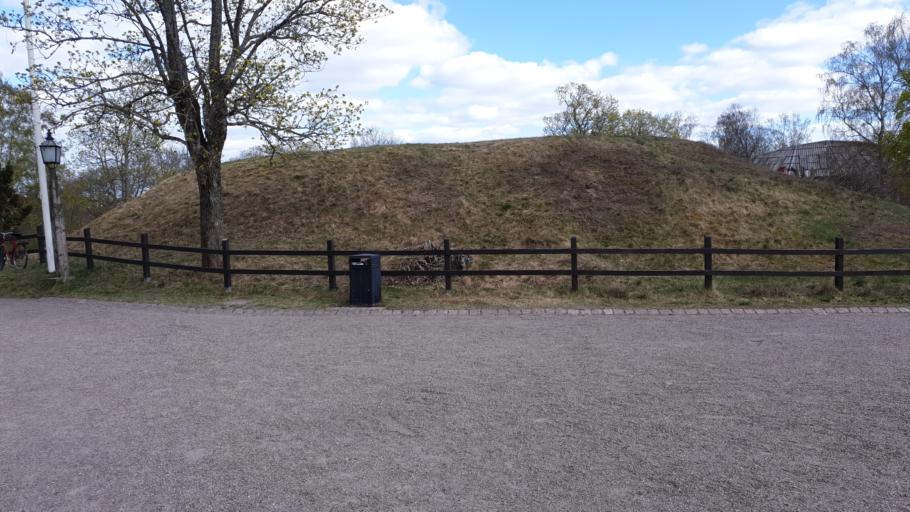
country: SE
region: Uppsala
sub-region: Uppsala Kommun
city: Gamla Uppsala
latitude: 59.8989
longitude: 17.6324
